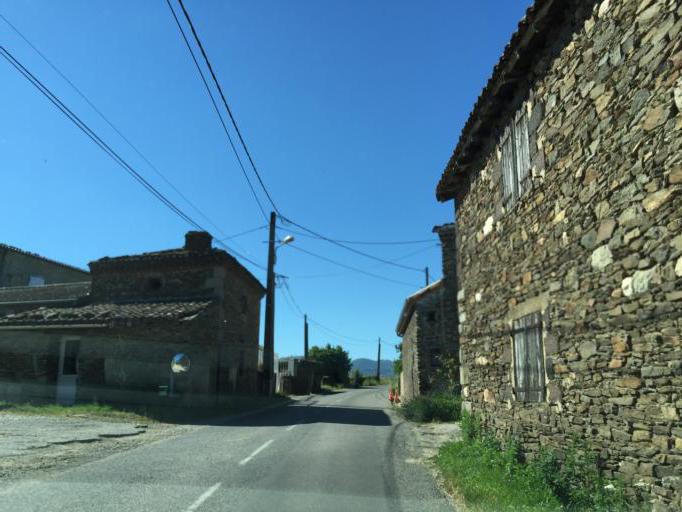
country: FR
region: Rhone-Alpes
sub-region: Departement du Rhone
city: Saint-Andeol-le-Chateau
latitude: 45.5694
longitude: 4.6760
